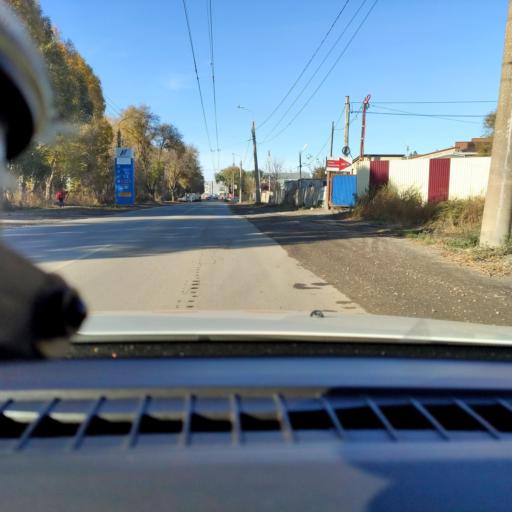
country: RU
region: Samara
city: Samara
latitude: 53.1995
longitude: 50.2674
